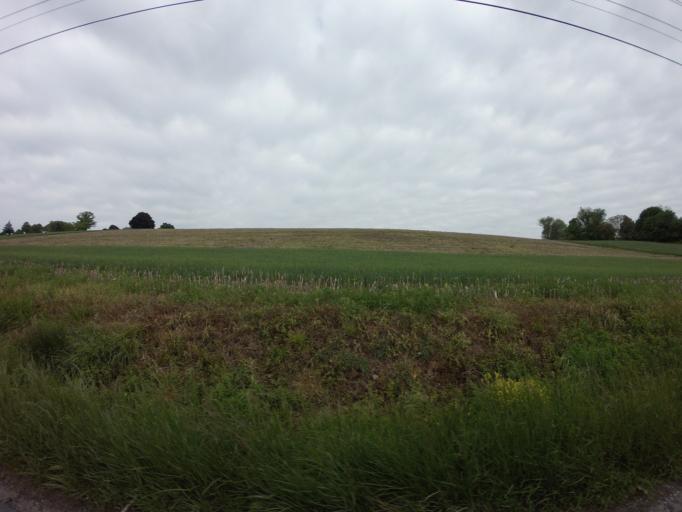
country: US
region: Maryland
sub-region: Frederick County
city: Green Valley
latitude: 39.3004
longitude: -77.2572
